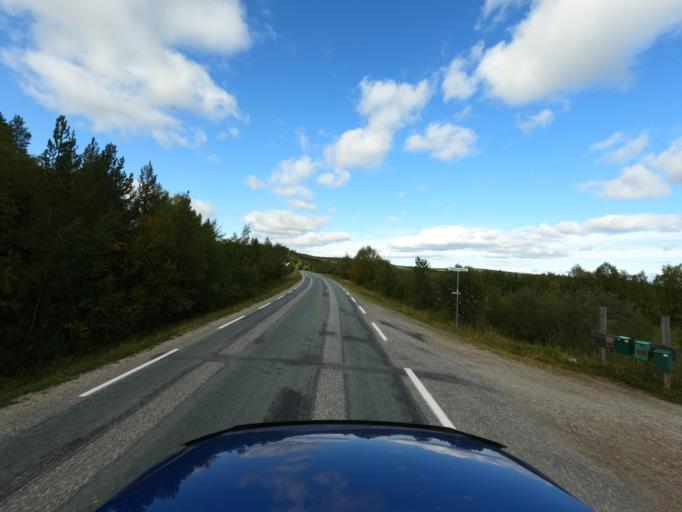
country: NO
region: Finnmark Fylke
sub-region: Karasjok
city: Karasjohka
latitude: 69.4126
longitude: 25.8025
